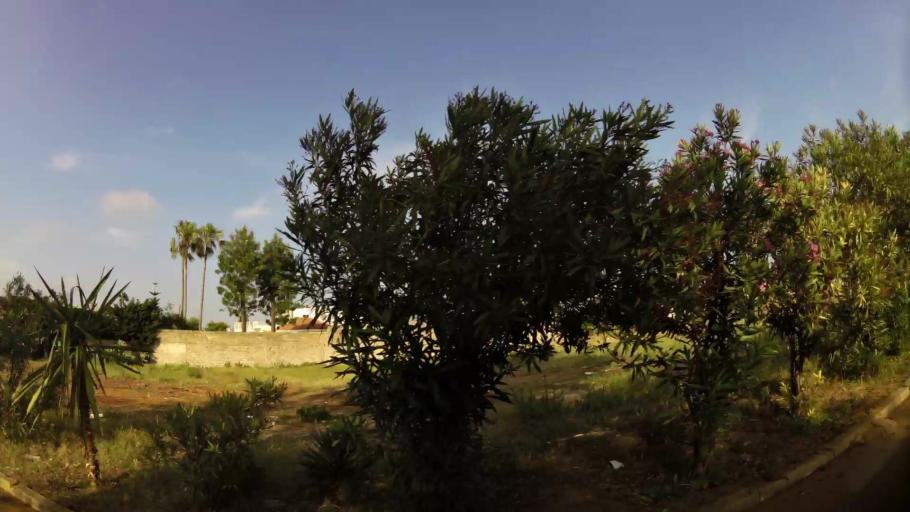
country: MA
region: Rabat-Sale-Zemmour-Zaer
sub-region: Rabat
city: Rabat
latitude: 33.9412
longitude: -6.8099
